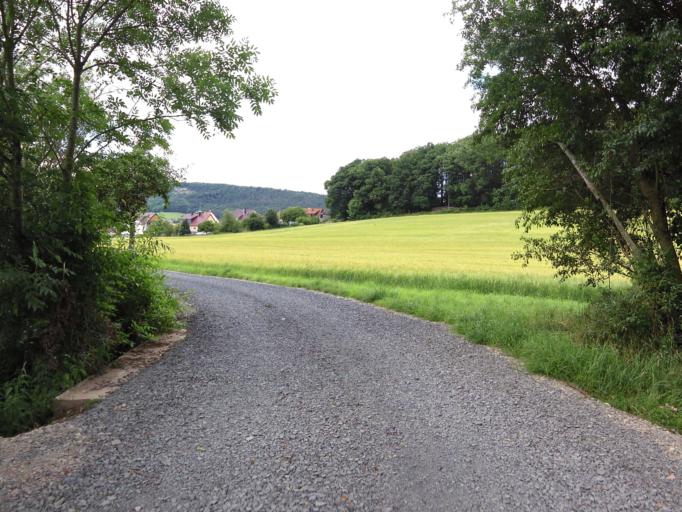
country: DE
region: Thuringia
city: Krauthausen
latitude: 50.9985
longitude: 10.2192
